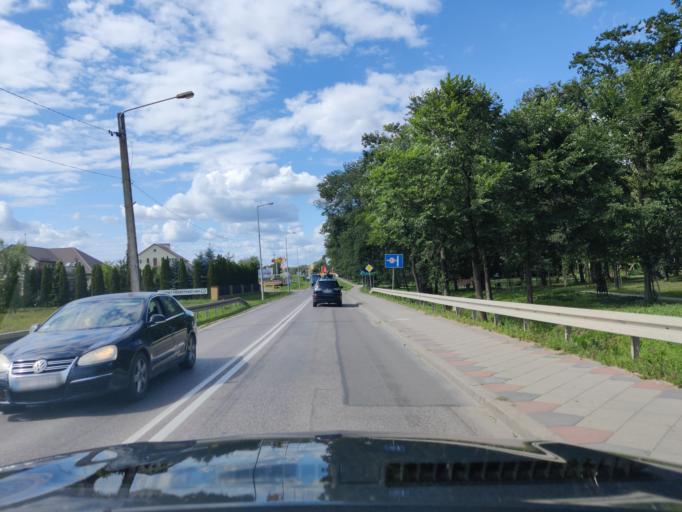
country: PL
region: Podlasie
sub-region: Powiat wysokomazowiecki
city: Czyzew
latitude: 52.8000
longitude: 22.3113
